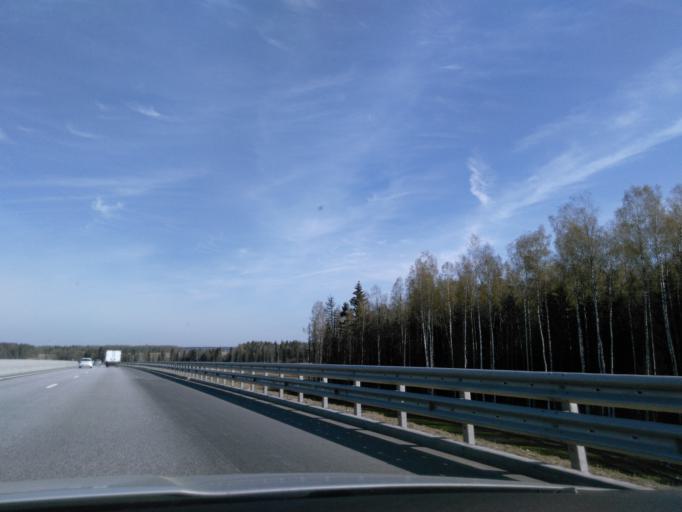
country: RU
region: Moskovskaya
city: Mendeleyevo
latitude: 56.0822
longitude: 37.2086
